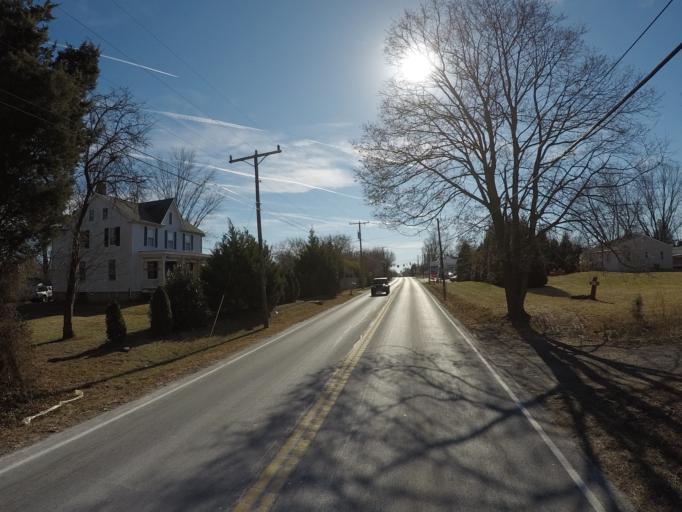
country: US
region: Maryland
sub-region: Frederick County
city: Point of Rocks
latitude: 39.2176
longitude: -77.5341
